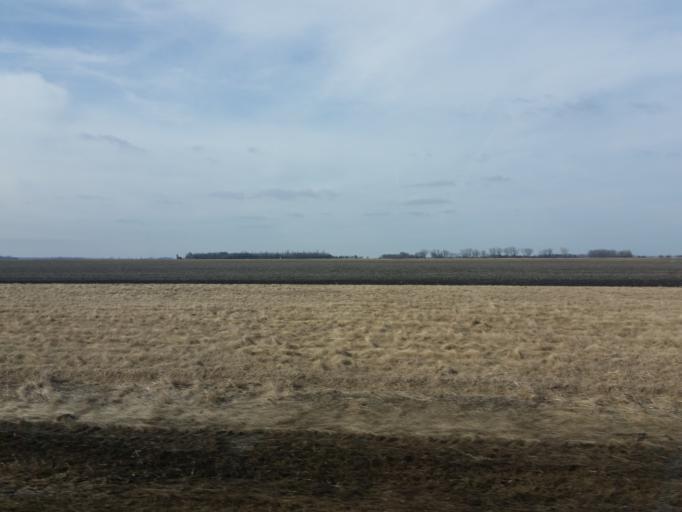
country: US
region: Minnesota
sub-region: Clay County
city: Barnesville
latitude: 46.4711
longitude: -96.4181
